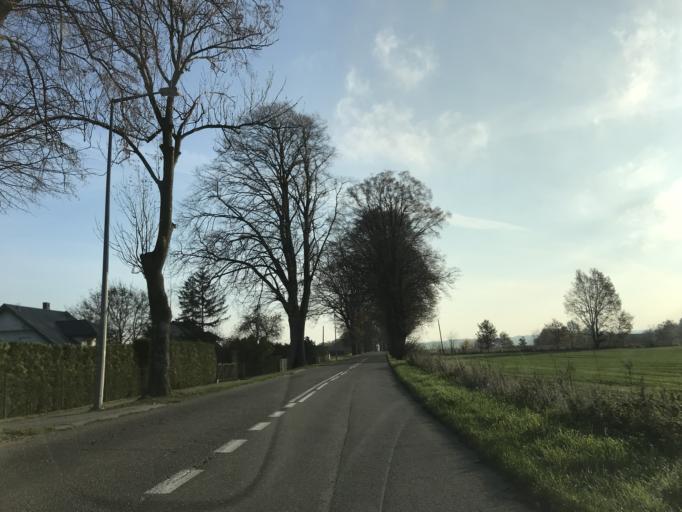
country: PL
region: Pomeranian Voivodeship
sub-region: Powiat pucki
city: Krokowa
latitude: 54.7848
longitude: 18.1366
